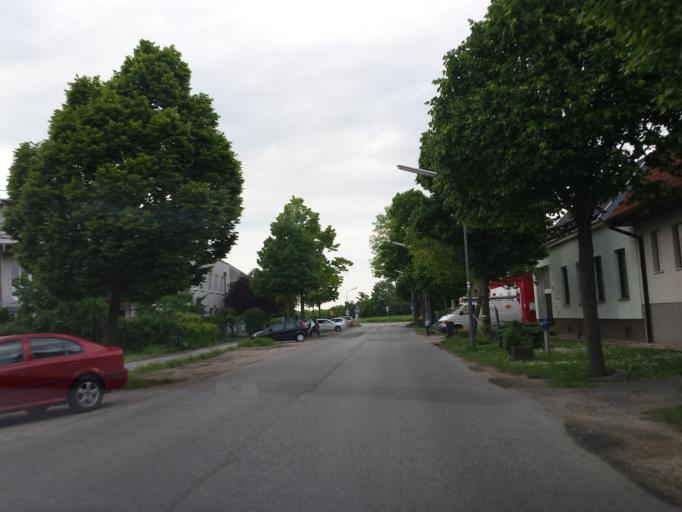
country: AT
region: Lower Austria
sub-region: Politischer Bezirk Ganserndorf
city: Gross-Enzersdorf
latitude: 48.2153
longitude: 16.5199
